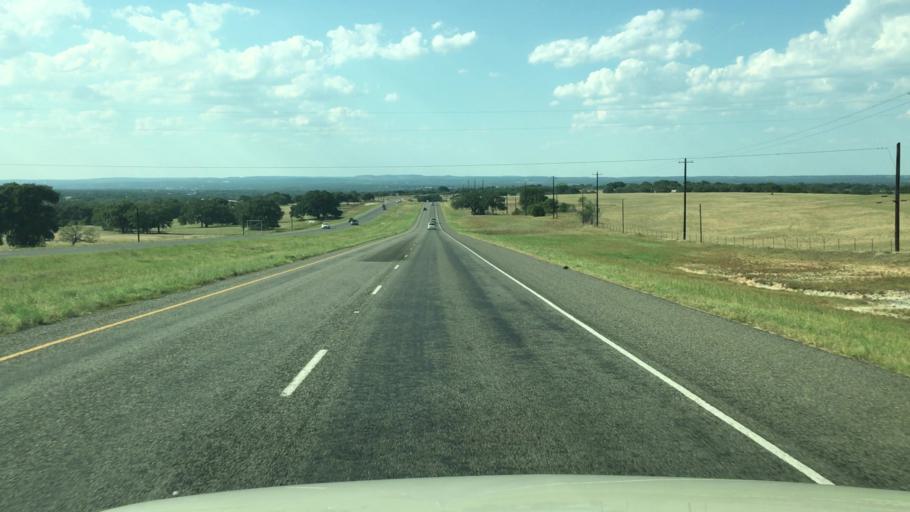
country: US
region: Texas
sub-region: Blanco County
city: Johnson City
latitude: 30.2392
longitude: -98.3861
